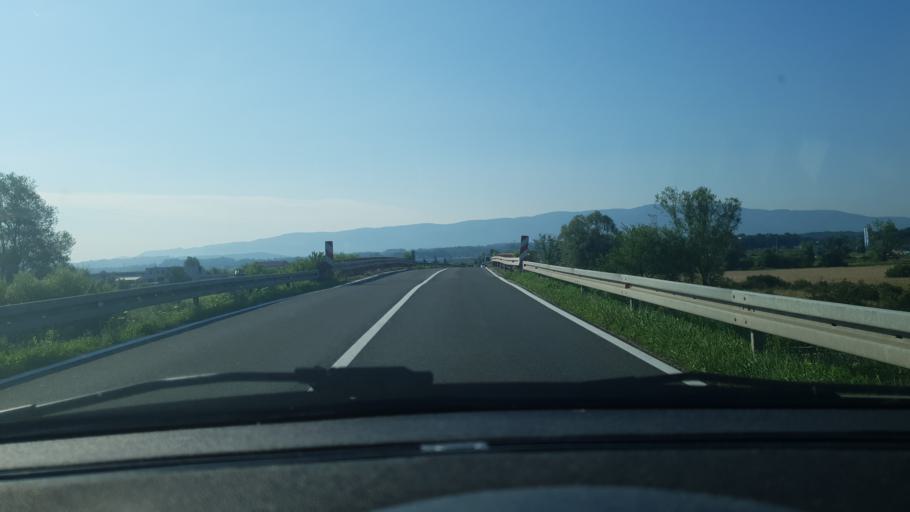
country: HR
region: Krapinsko-Zagorska
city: Oroslavje
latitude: 46.0125
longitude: 15.8736
